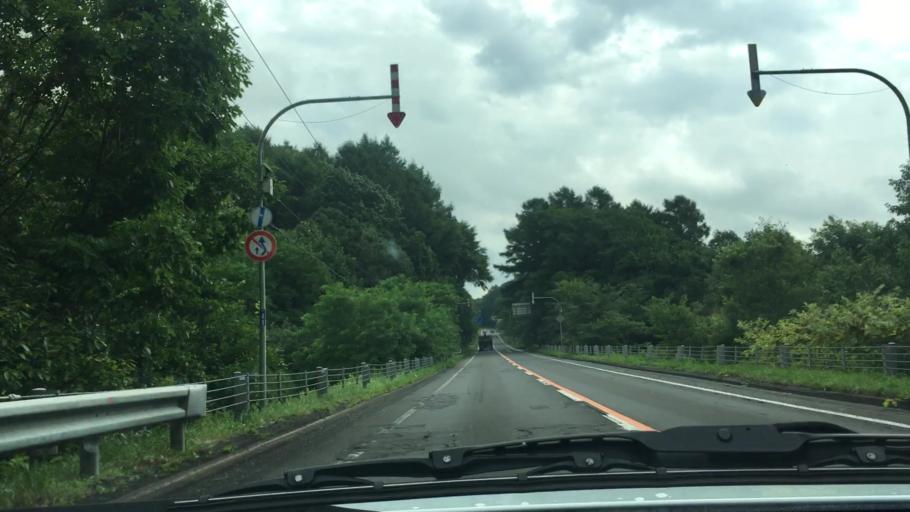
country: JP
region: Hokkaido
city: Chitose
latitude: 42.9452
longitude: 141.7404
